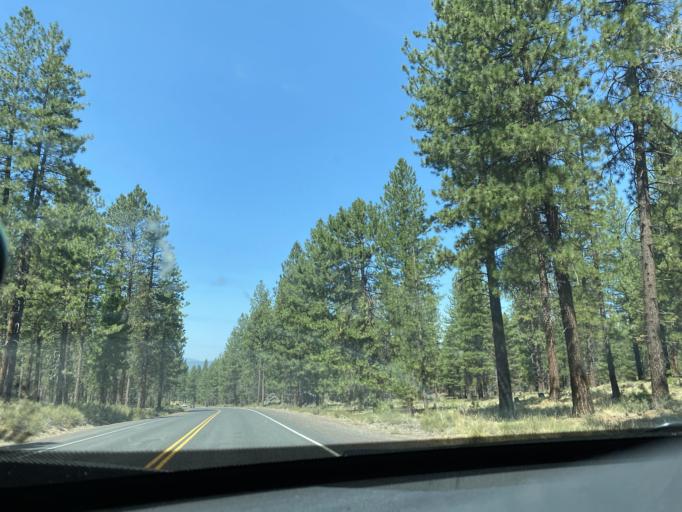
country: US
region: Oregon
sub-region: Deschutes County
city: Sunriver
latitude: 43.8897
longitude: -121.4006
